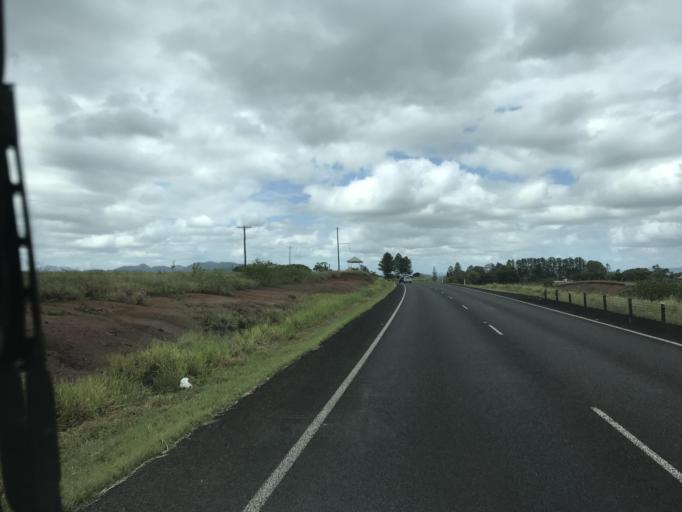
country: AU
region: Queensland
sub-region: Cassowary Coast
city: Innisfail
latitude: -17.5781
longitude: 145.9710
